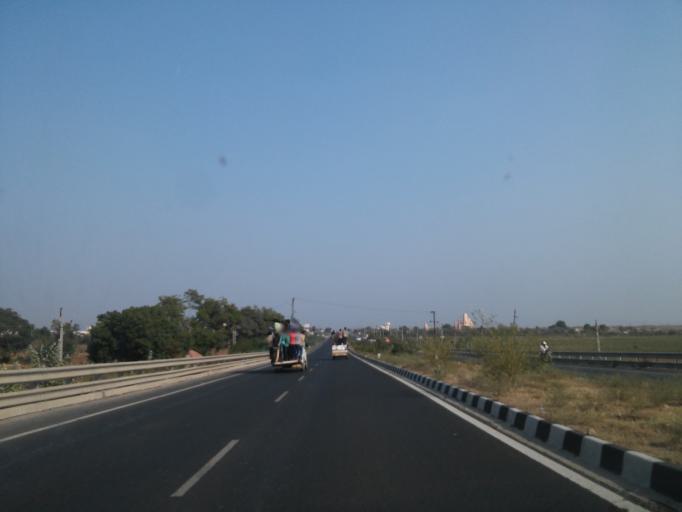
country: IN
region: Gujarat
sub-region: Surendranagar
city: Halvad
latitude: 23.0118
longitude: 71.2260
